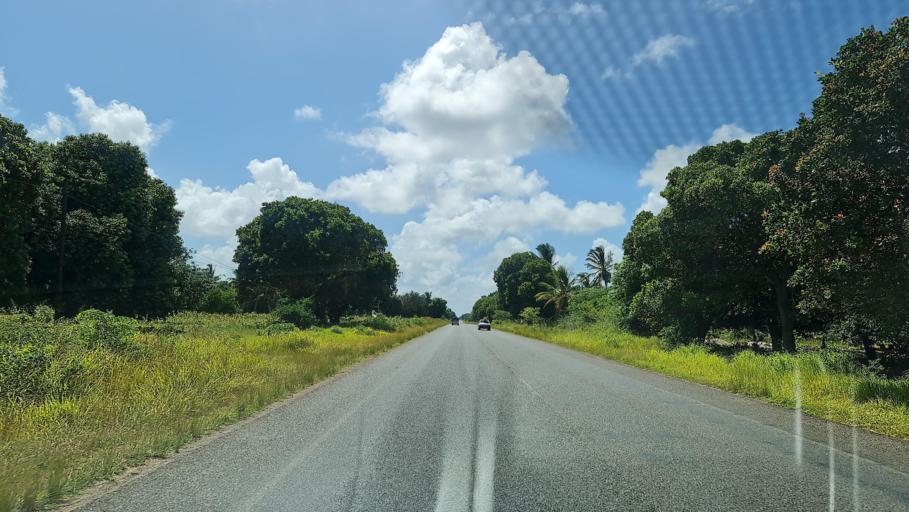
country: MZ
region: Inhambane
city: Maxixe
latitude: -24.5418
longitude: 34.9070
